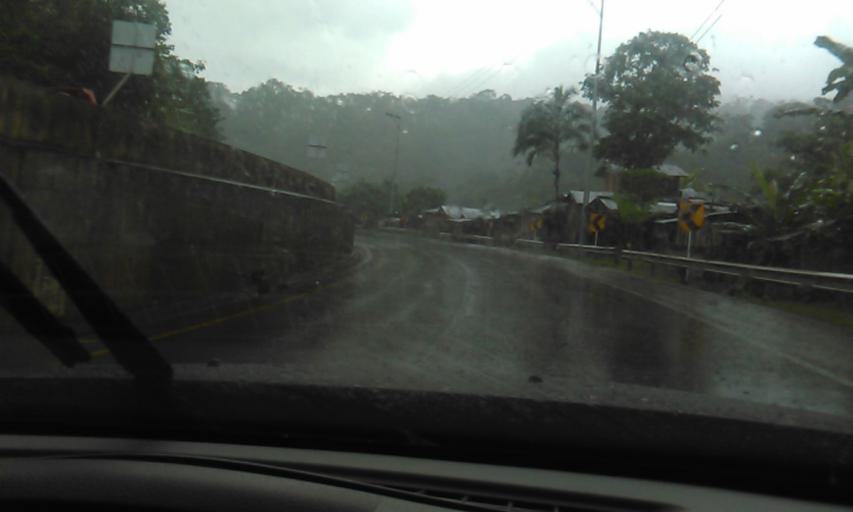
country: CO
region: Valle del Cauca
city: Buenaventura
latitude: 3.8607
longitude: -76.8336
